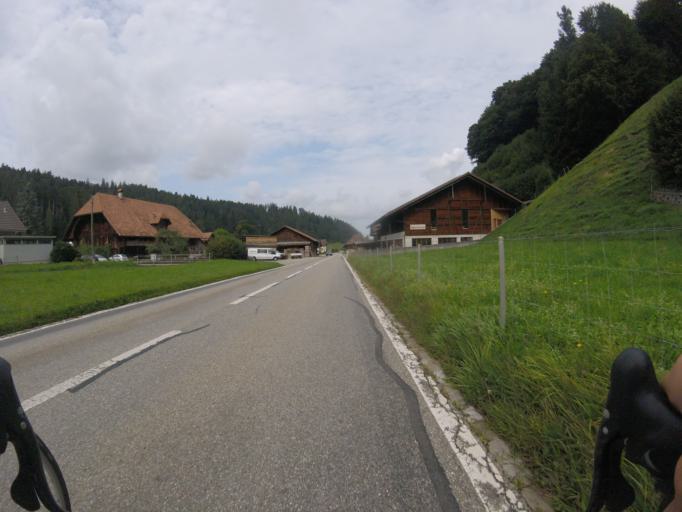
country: CH
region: Bern
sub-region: Emmental District
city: Lutzelfluh
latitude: 46.9941
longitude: 7.6843
